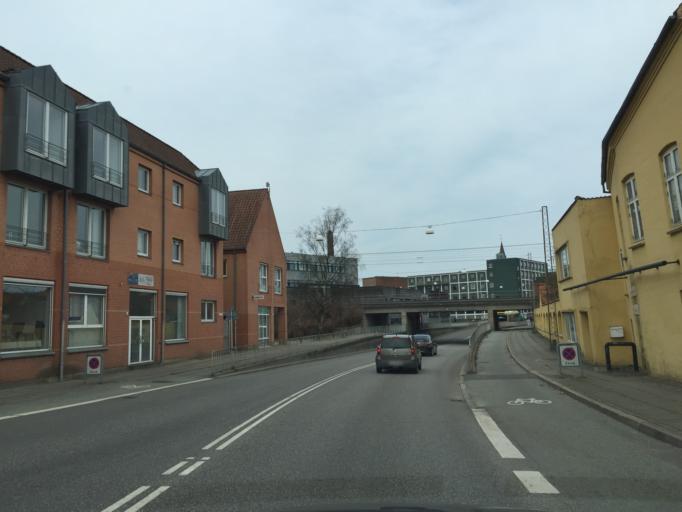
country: DK
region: South Denmark
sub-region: Kolding Kommune
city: Kolding
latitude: 55.4870
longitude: 9.4719
